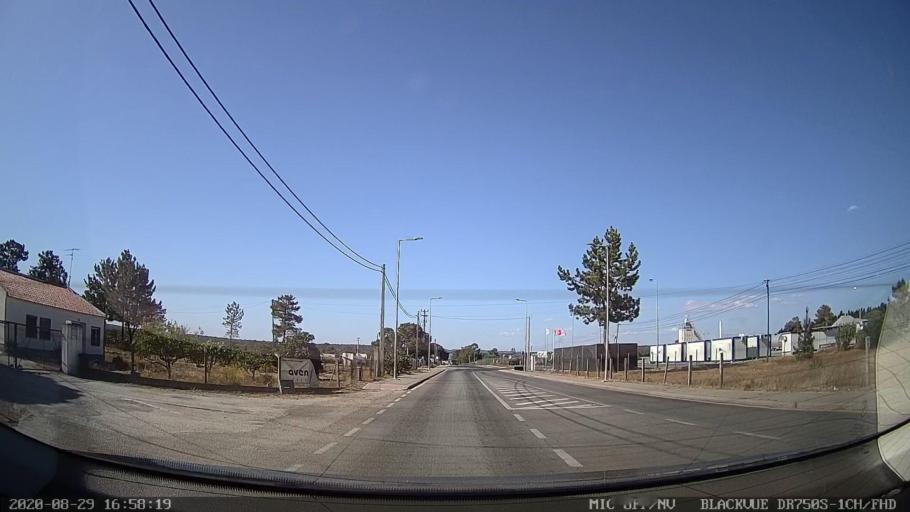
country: PT
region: Setubal
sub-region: Alcacer do Sal
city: Alcacer do Sal
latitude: 38.3965
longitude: -8.5144
